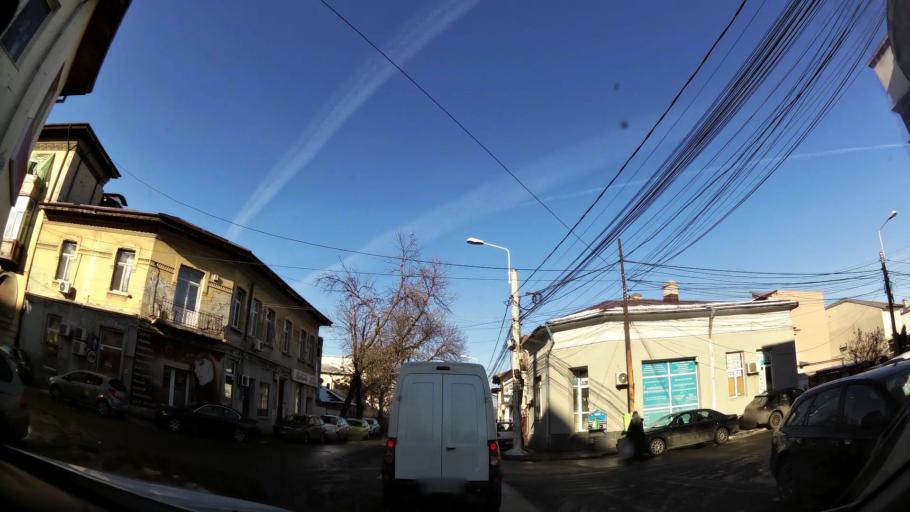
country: RO
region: Bucuresti
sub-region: Municipiul Bucuresti
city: Bucharest
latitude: 44.4319
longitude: 26.1207
